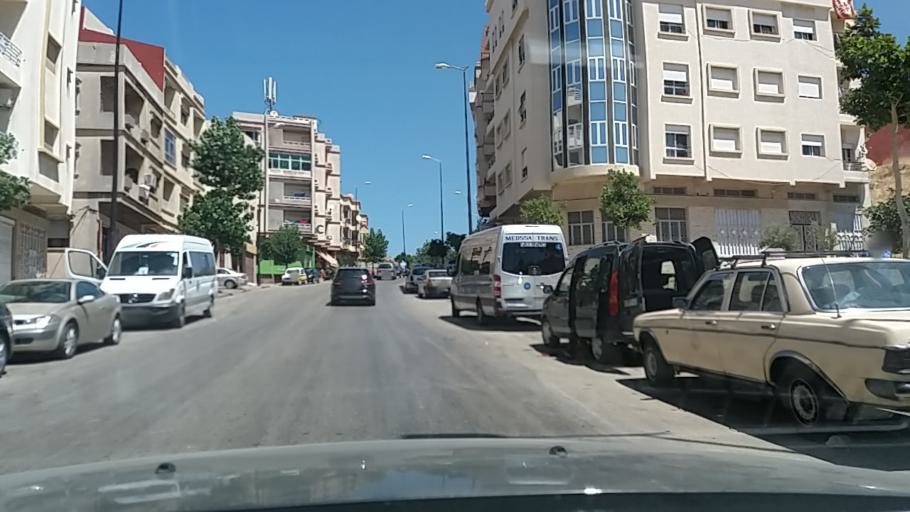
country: MA
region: Tanger-Tetouan
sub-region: Tanger-Assilah
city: Tangier
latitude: 35.7658
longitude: -5.7941
